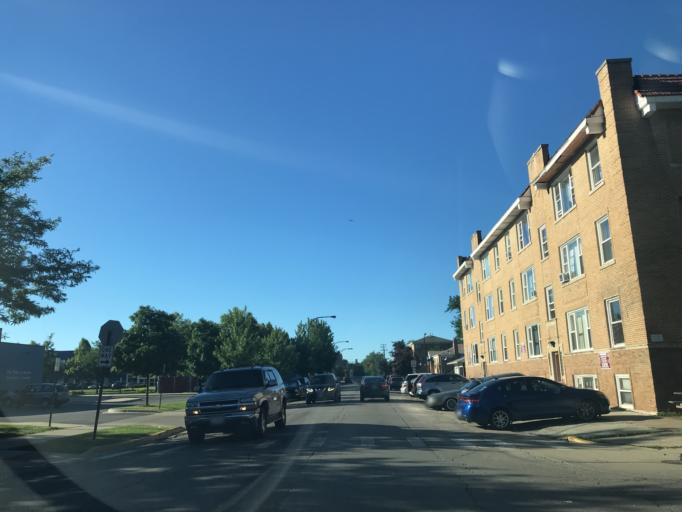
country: US
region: Illinois
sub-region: Cook County
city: Cicero
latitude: 41.8491
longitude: -87.7467
